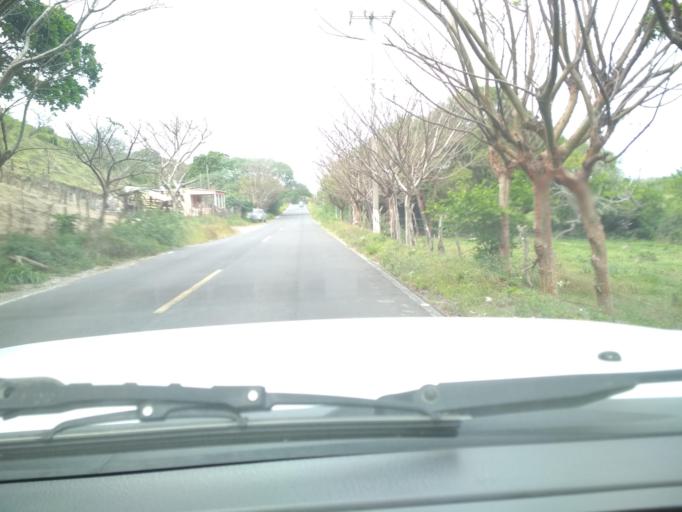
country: MX
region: Veracruz
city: Anton Lizardo
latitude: 19.0422
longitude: -95.9860
